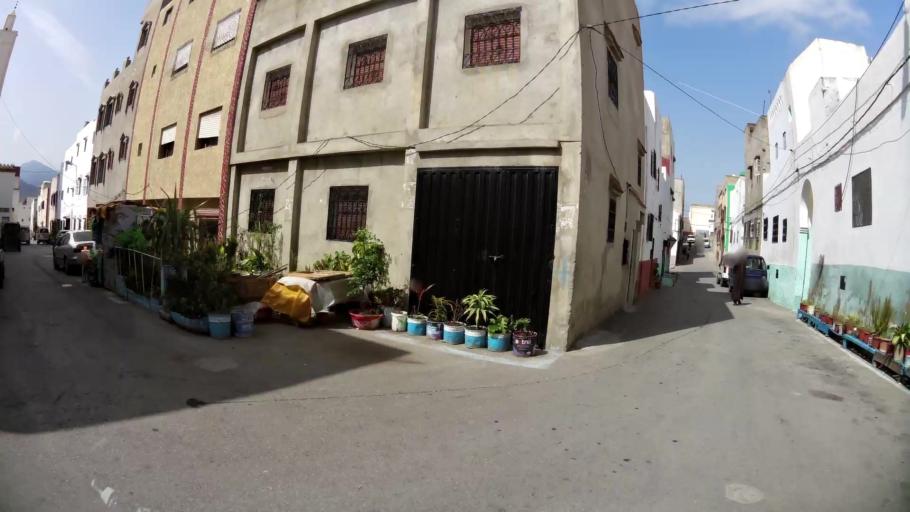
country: MA
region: Tanger-Tetouan
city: Tetouan
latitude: 35.5778
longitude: -5.3845
